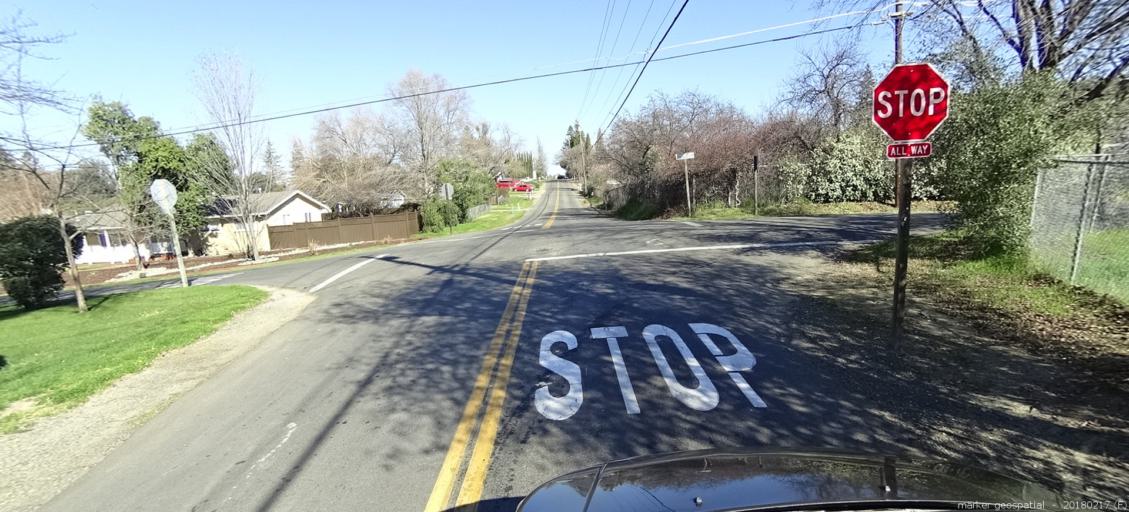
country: US
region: California
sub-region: Sacramento County
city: Orangevale
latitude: 38.7069
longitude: -121.2020
